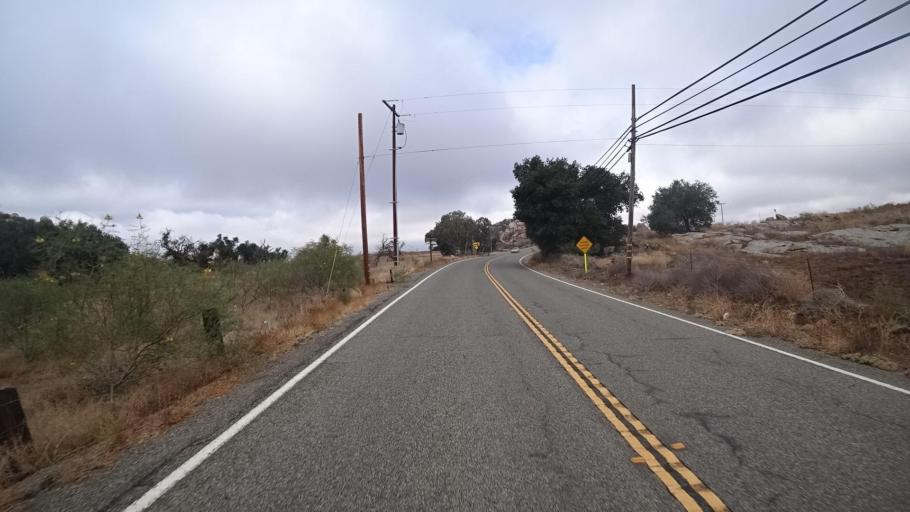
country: MX
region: Baja California
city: Tecate
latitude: 32.6002
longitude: -116.5893
